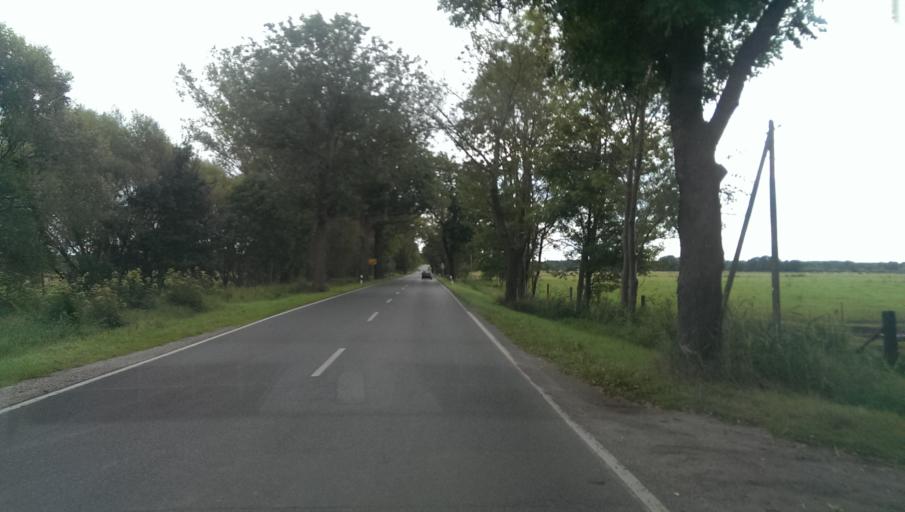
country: DE
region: Brandenburg
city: Velten
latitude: 52.6486
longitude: 13.1448
